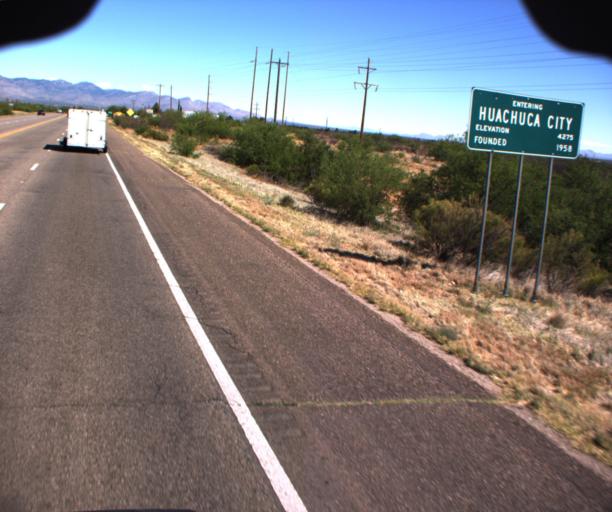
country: US
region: Arizona
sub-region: Cochise County
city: Huachuca City
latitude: 31.6137
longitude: -110.3334
